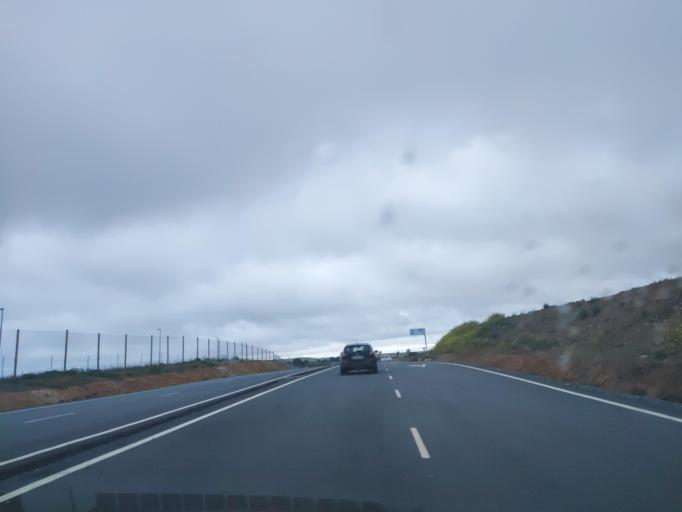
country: ES
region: Castille-La Mancha
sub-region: Province of Toledo
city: Toledo
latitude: 39.8409
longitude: -4.0851
